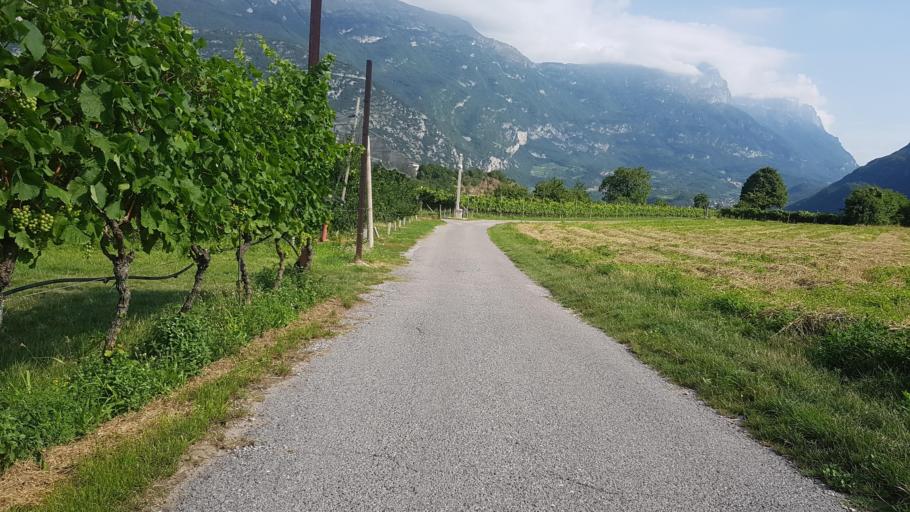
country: IT
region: Trentino-Alto Adige
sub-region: Provincia di Trento
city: Calavino
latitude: 46.0425
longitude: 10.9783
